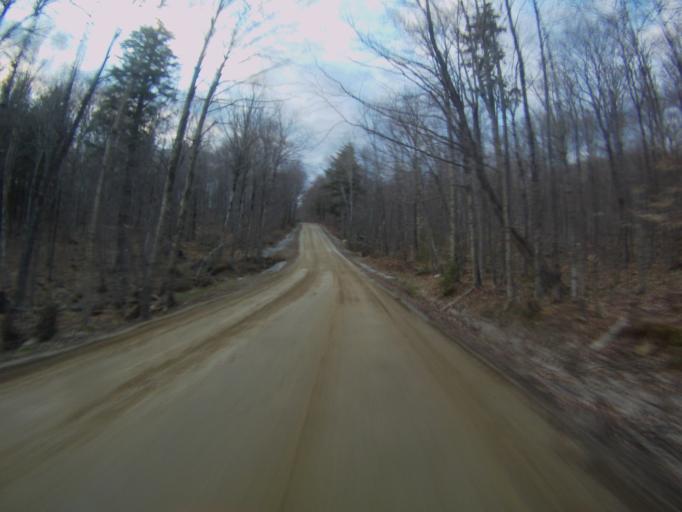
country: US
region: Vermont
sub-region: Rutland County
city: Brandon
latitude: 43.9212
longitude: -73.0184
